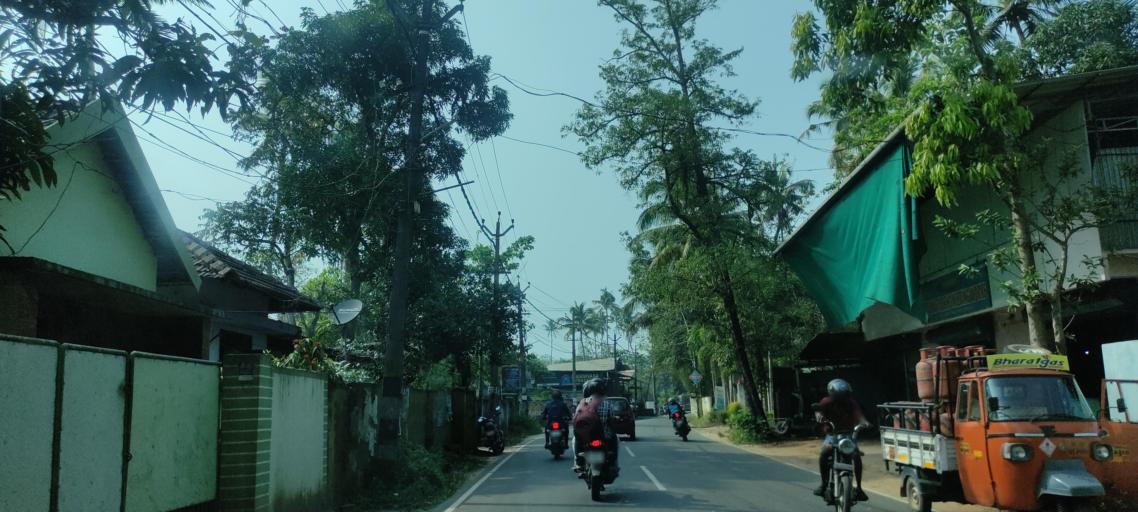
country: IN
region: Kerala
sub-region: Alappuzha
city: Vayalar
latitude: 9.6939
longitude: 76.3311
